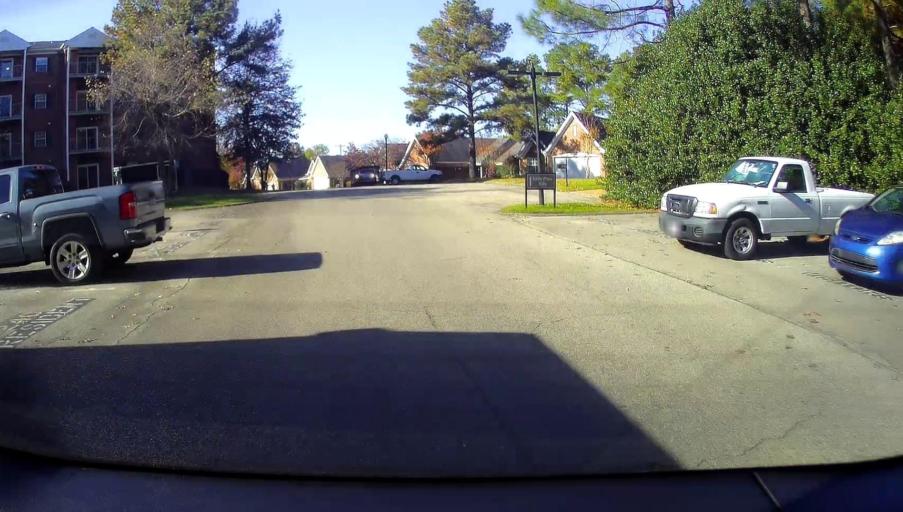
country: US
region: Tennessee
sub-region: Shelby County
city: Germantown
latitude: 35.0550
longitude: -89.8473
